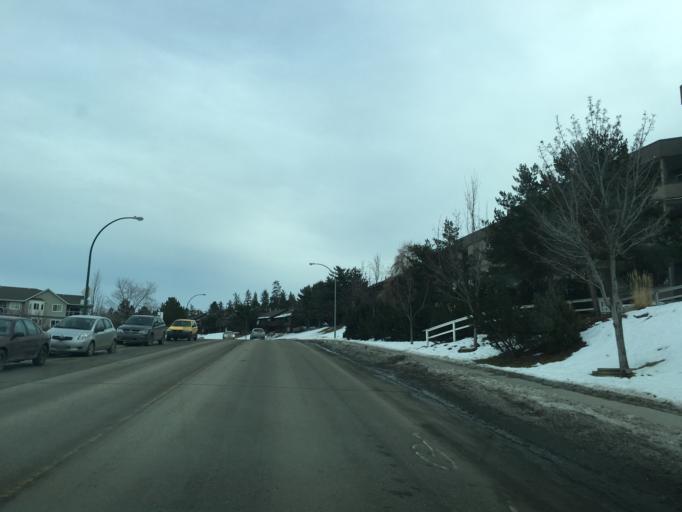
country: CA
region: British Columbia
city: Kamloops
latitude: 50.6494
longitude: -120.3721
